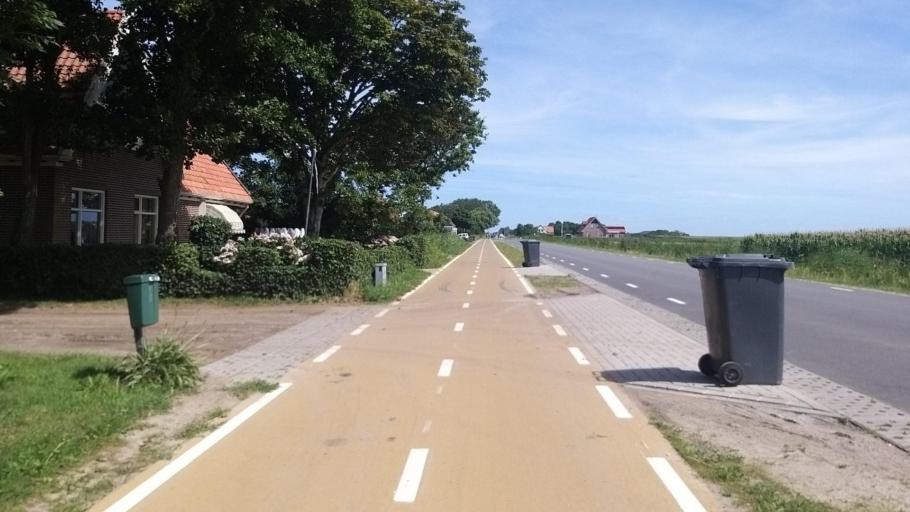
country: NL
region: North Holland
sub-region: Gemeente Texel
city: Den Burg
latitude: 53.1061
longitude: 4.8123
